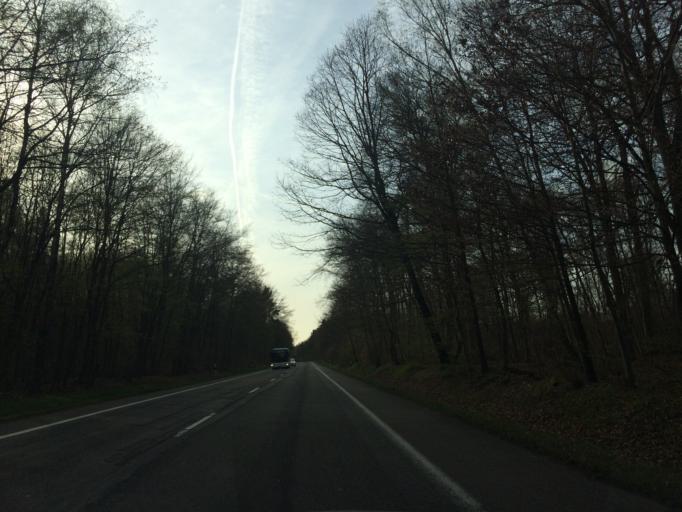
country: DE
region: Hesse
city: Langen
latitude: 50.0278
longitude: 8.6347
